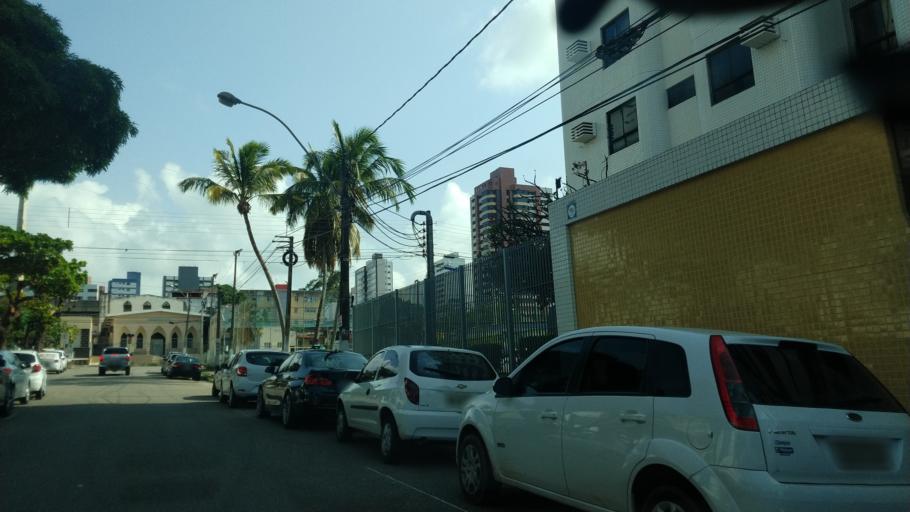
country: BR
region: Rio Grande do Norte
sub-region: Natal
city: Natal
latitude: -5.7996
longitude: -35.2031
